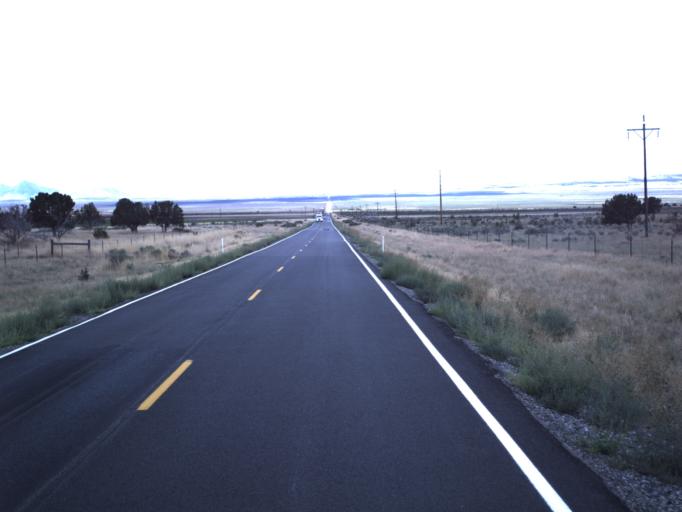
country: US
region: Utah
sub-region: Tooele County
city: Grantsville
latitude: 40.3068
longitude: -112.6421
